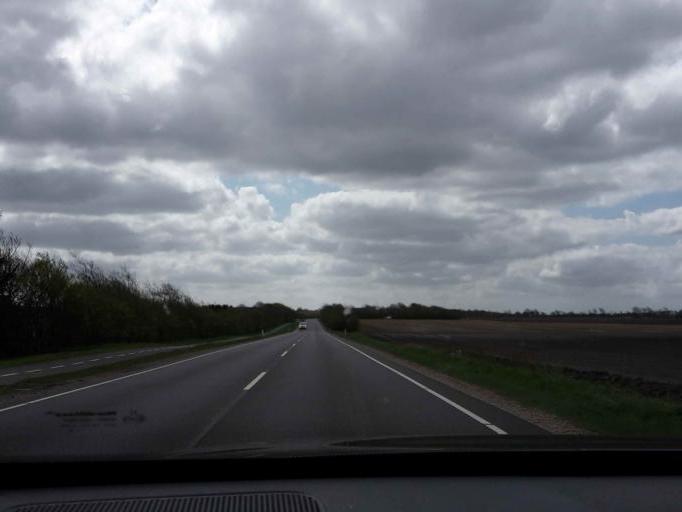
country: DK
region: South Denmark
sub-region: Varde Kommune
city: Olgod
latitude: 55.7398
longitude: 8.6180
